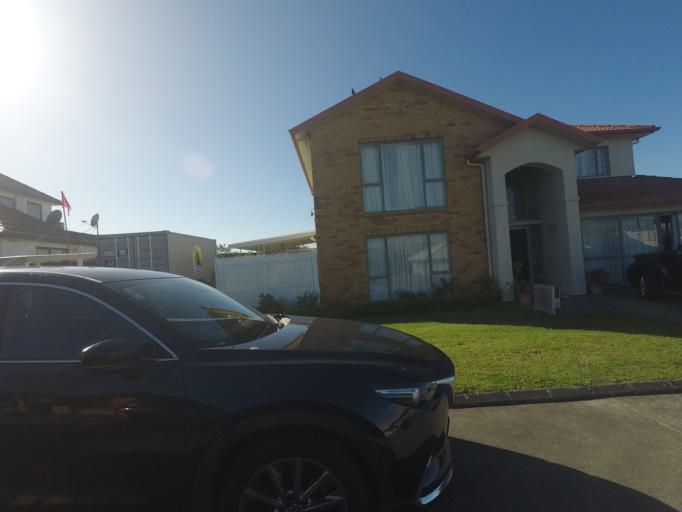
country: NZ
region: Auckland
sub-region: Auckland
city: Rosebank
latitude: -36.8997
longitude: 174.6861
